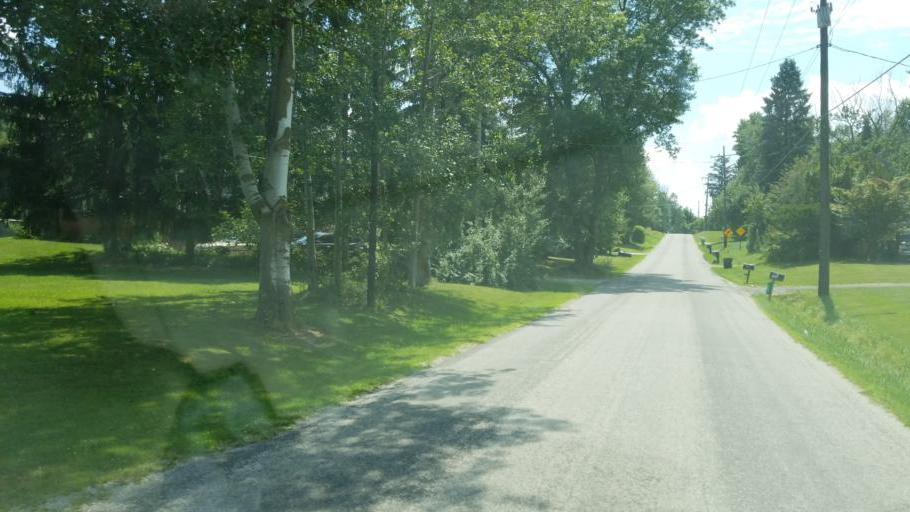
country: US
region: Ohio
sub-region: Richland County
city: Ontario
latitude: 40.7880
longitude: -82.6135
